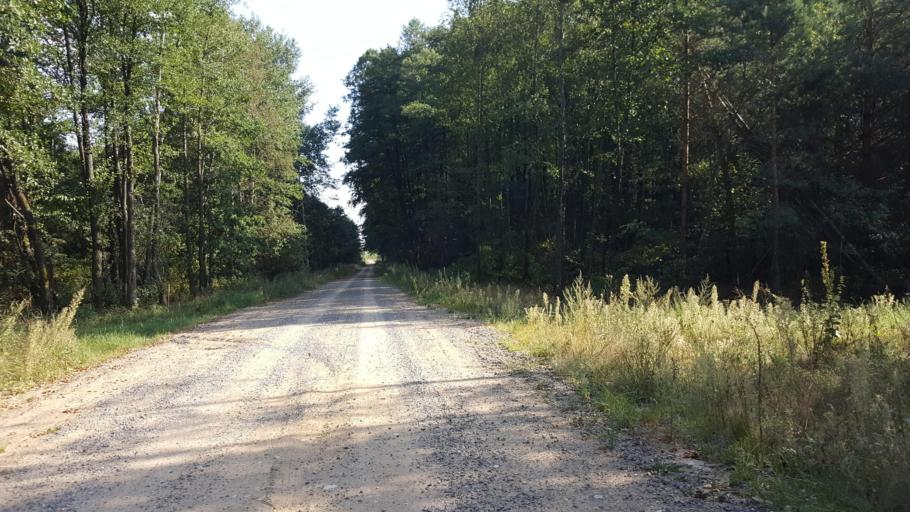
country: BY
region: Brest
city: Kamyanyuki
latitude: 52.5667
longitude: 23.6298
